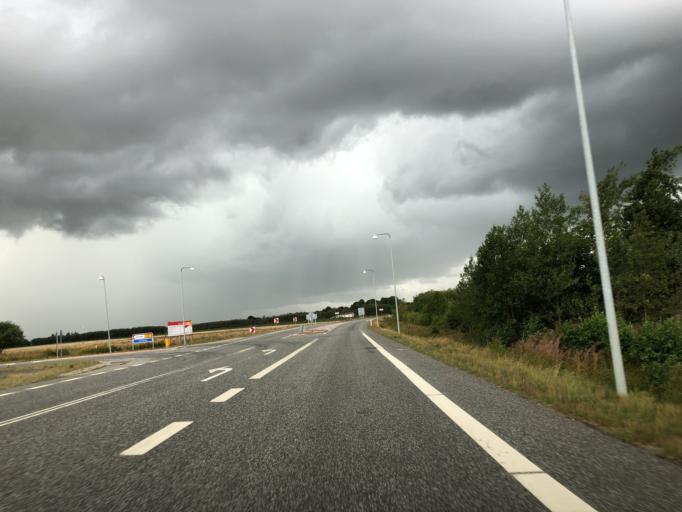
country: DK
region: Central Jutland
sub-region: Ikast-Brande Kommune
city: Bording Kirkeby
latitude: 56.1369
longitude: 9.3442
